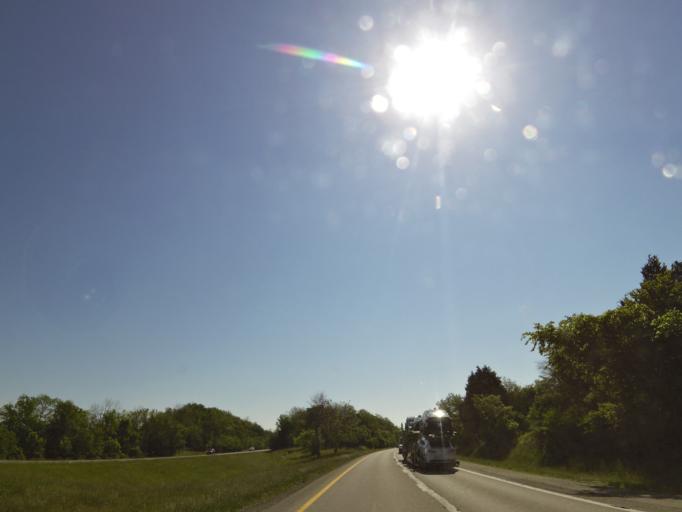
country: US
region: Kentucky
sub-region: Franklin County
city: Frankfort
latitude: 38.1516
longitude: -84.9514
